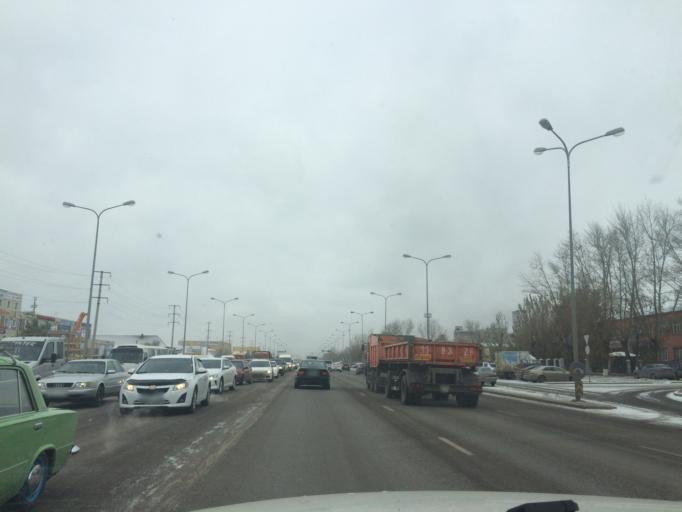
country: KZ
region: Astana Qalasy
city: Astana
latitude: 51.1793
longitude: 71.4672
